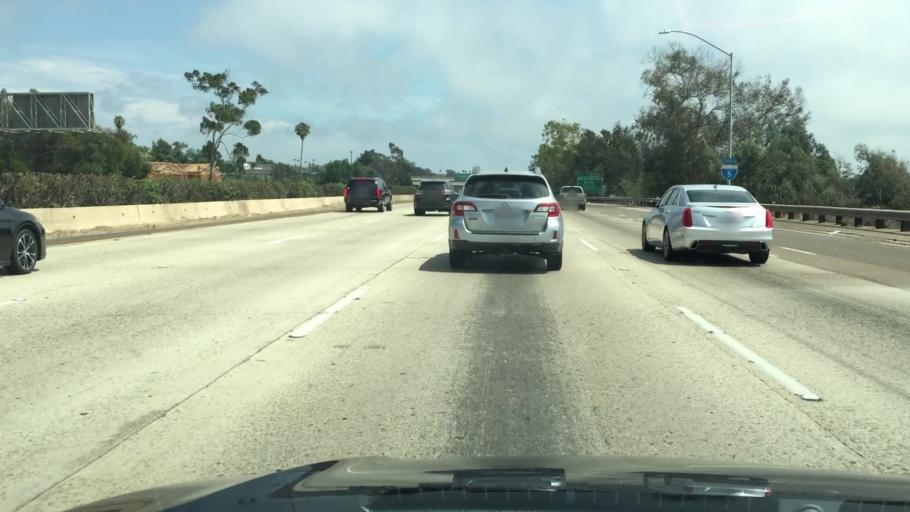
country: US
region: California
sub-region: San Diego County
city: Encinitas
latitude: 33.0335
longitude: -117.2798
